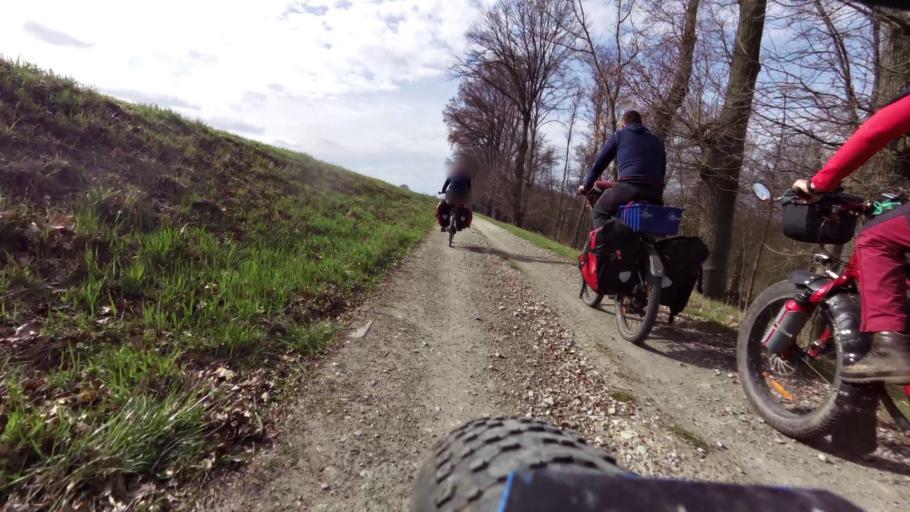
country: PL
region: Lubusz
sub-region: Powiat slubicki
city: Gorzyca
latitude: 52.5075
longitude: 14.6223
